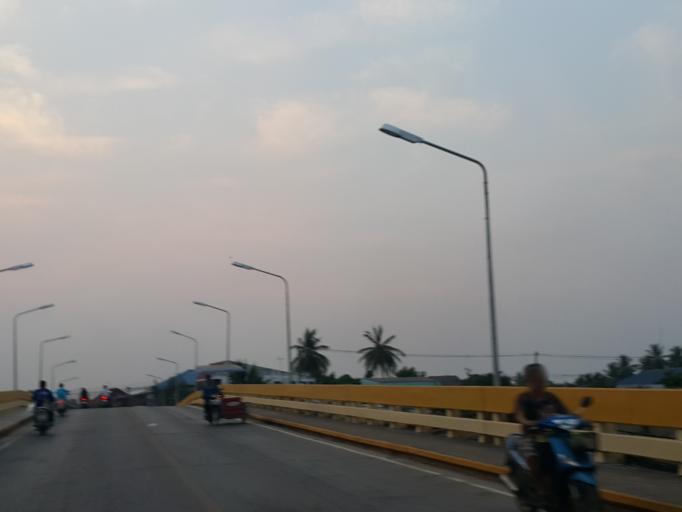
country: TH
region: Sukhothai
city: Sawankhalok
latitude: 17.3124
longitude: 99.8272
